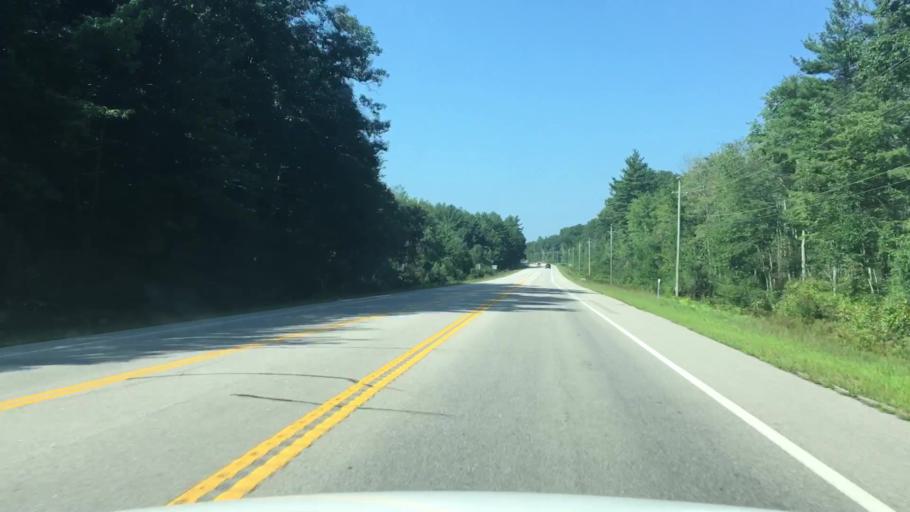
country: US
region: New Hampshire
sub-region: Rockingham County
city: Danville
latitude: 42.8958
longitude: -71.1282
